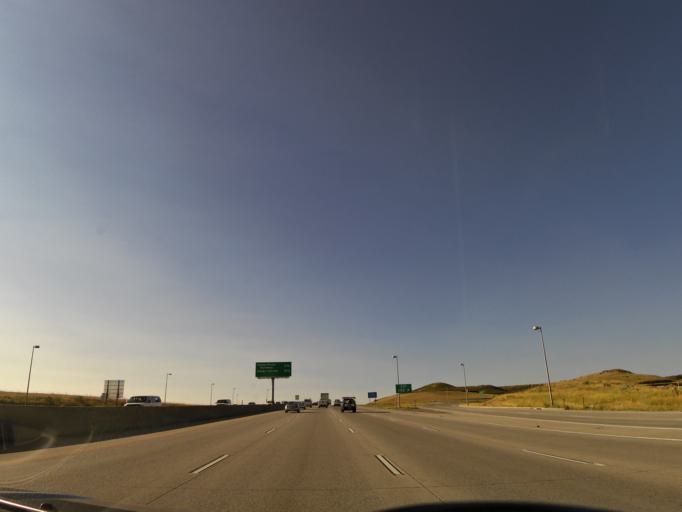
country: US
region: Colorado
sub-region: Douglas County
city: Meridian
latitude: 39.5274
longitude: -104.8678
